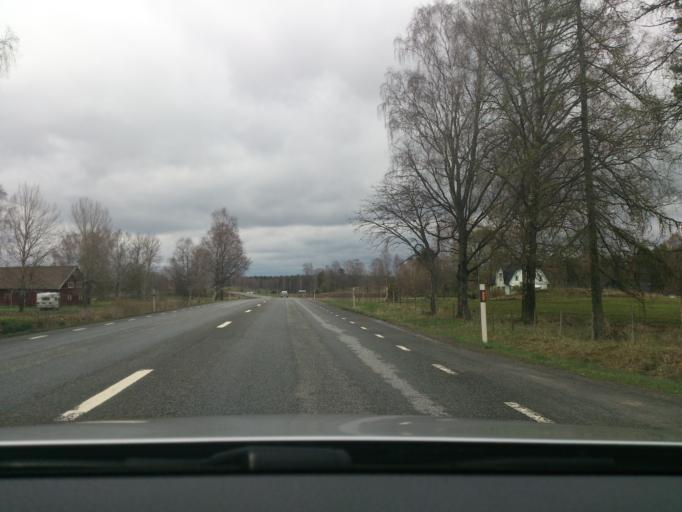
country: SE
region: Vaestra Goetaland
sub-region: Ulricehamns Kommun
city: Ulricehamn
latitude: 57.9643
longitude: 13.5263
